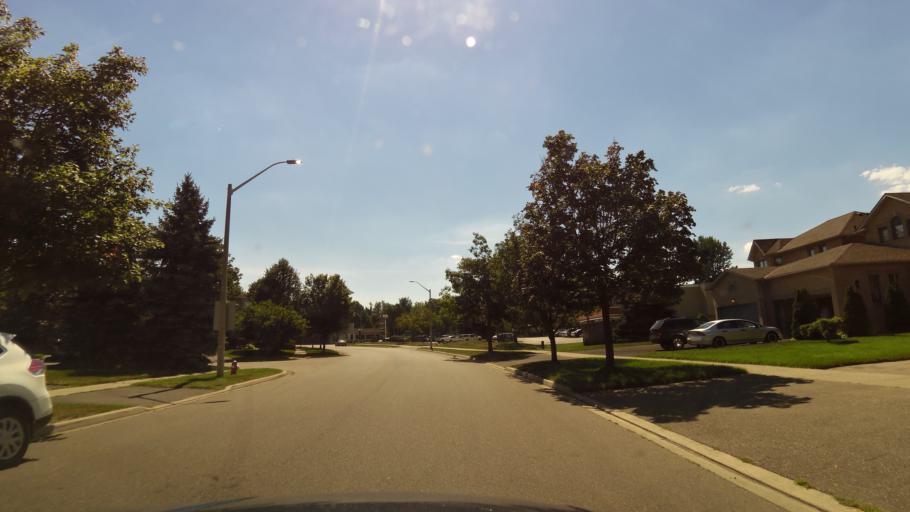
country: CA
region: Ontario
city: Mississauga
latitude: 43.5329
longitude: -79.6112
